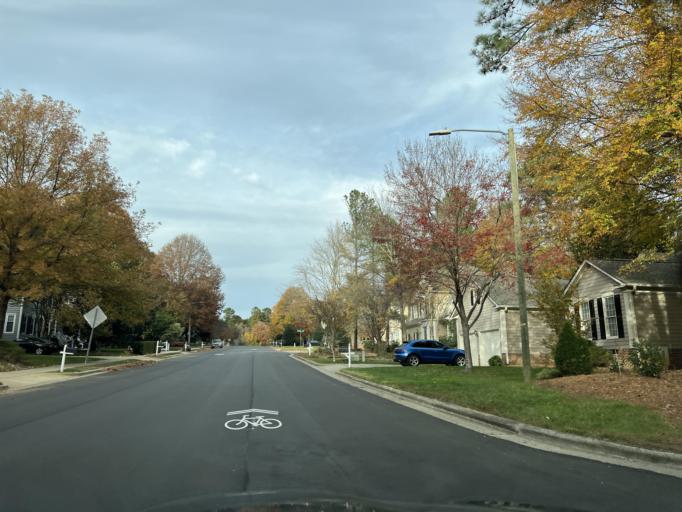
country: US
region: North Carolina
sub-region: Wake County
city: Wake Forest
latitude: 35.8989
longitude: -78.5874
